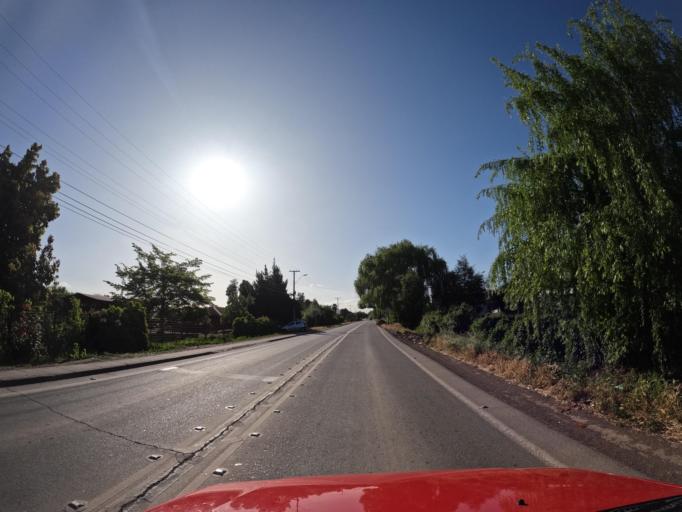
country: CL
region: Maule
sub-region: Provincia de Curico
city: Teno
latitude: -34.7421
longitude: -71.2480
